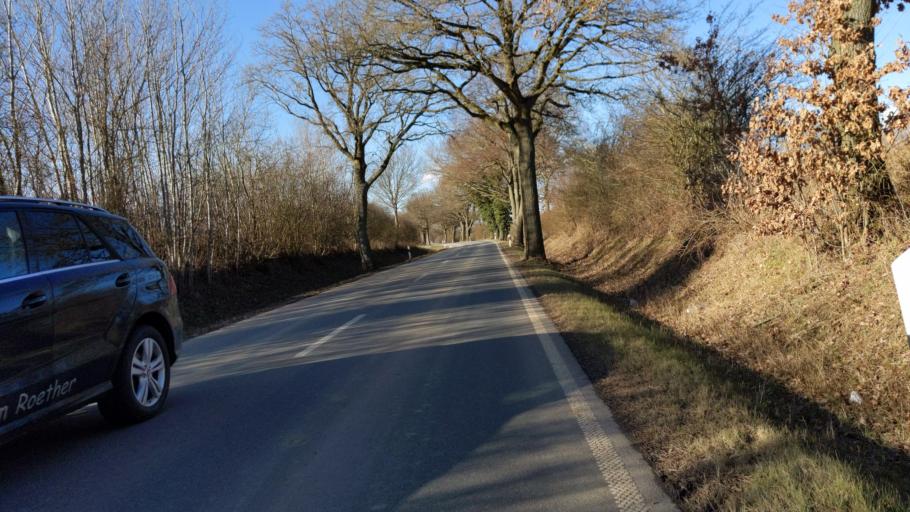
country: DE
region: Schleswig-Holstein
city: Susel
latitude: 54.0573
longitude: 10.6513
